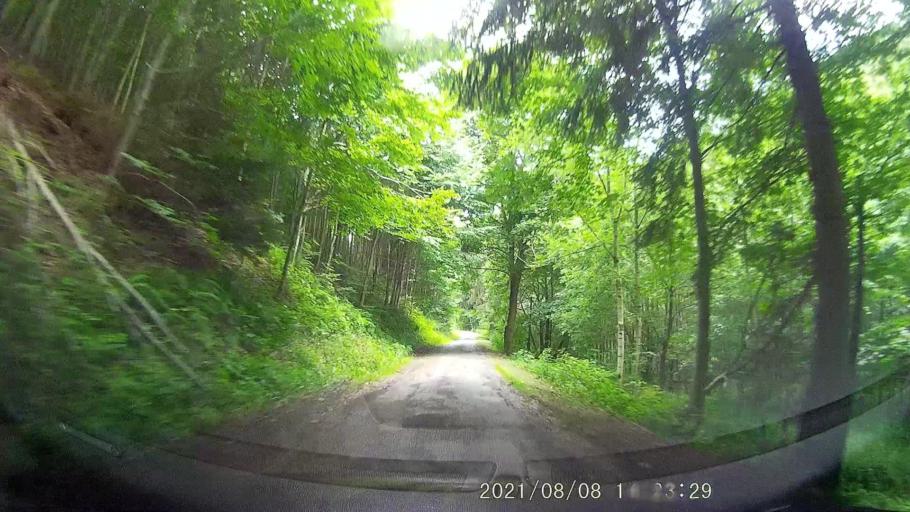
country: PL
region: Lower Silesian Voivodeship
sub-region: Powiat klodzki
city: Lewin Klodzki
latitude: 50.4419
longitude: 16.3032
